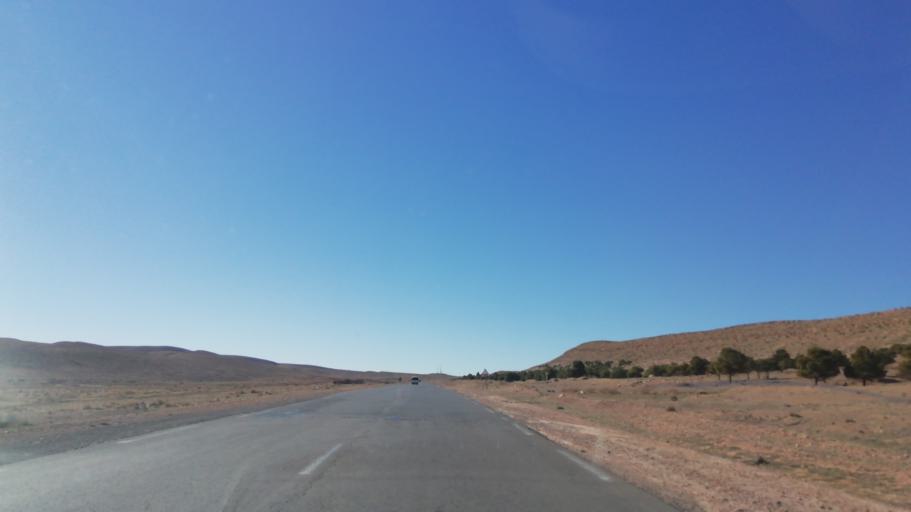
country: DZ
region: El Bayadh
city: El Bayadh
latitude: 33.6814
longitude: 1.4540
